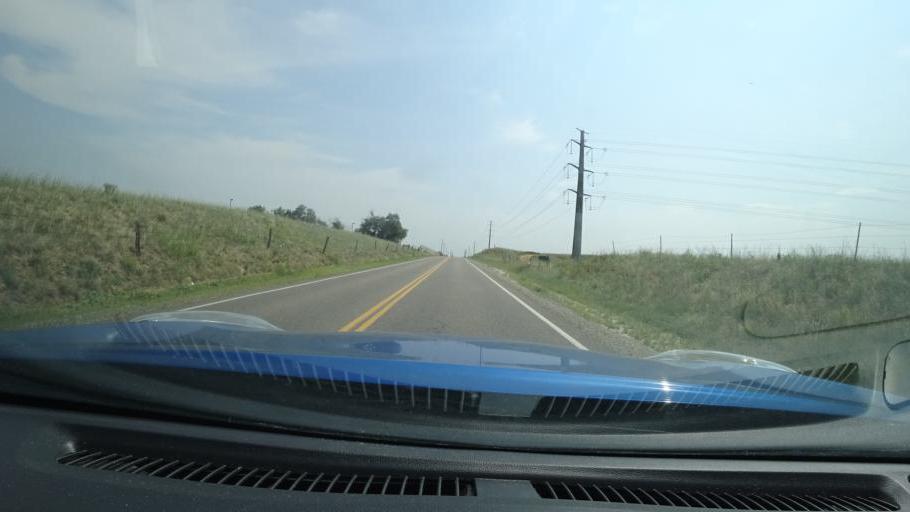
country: US
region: Colorado
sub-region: Adams County
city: Aurora
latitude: 39.7666
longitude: -104.7346
